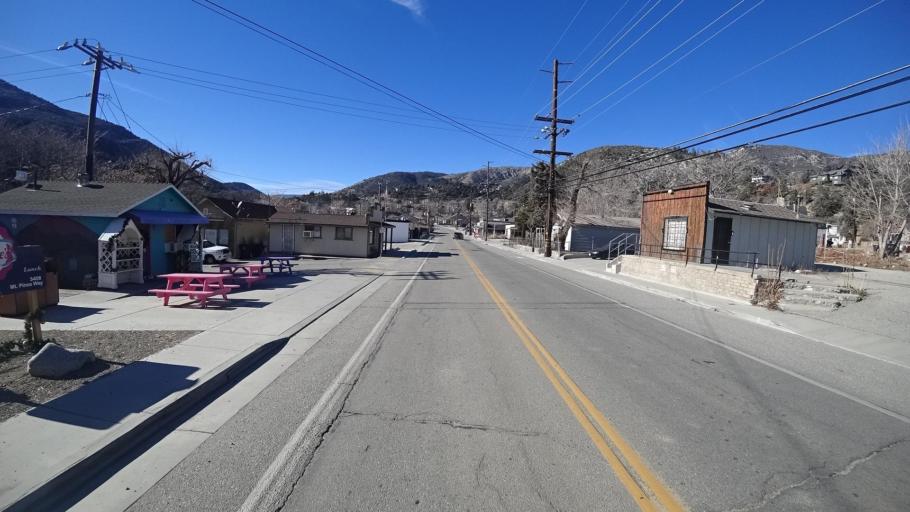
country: US
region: California
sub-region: Kern County
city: Frazier Park
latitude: 34.8219
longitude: -118.9422
